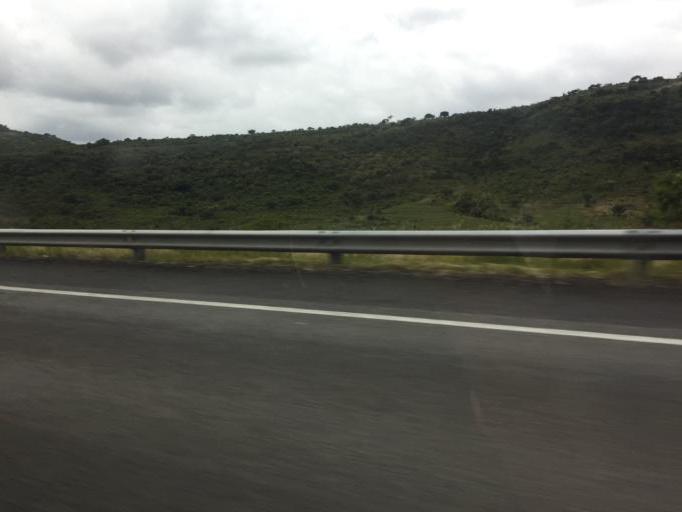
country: MX
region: Jalisco
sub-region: Zapotlan del Rey
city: Zapotlan del Rey
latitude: 20.5195
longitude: -102.9882
